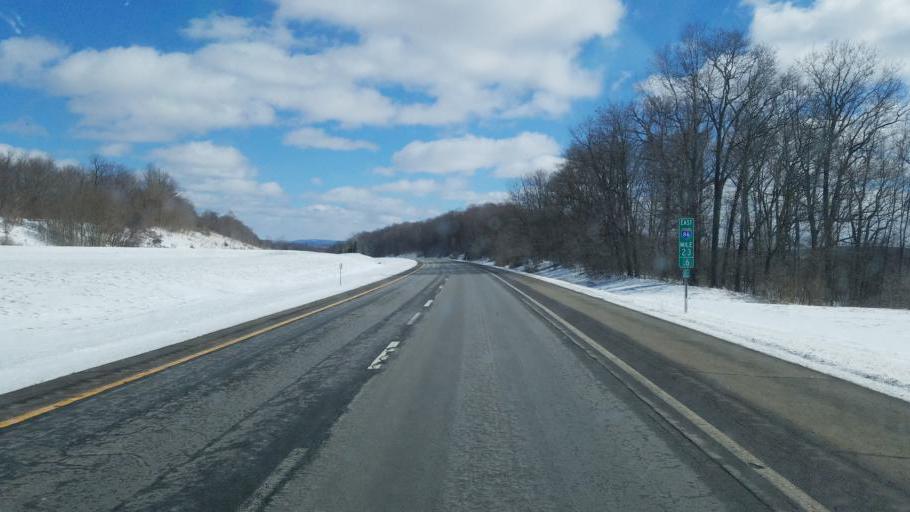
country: US
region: New York
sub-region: Chautauqua County
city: Lakewood
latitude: 42.1303
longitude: -79.3253
